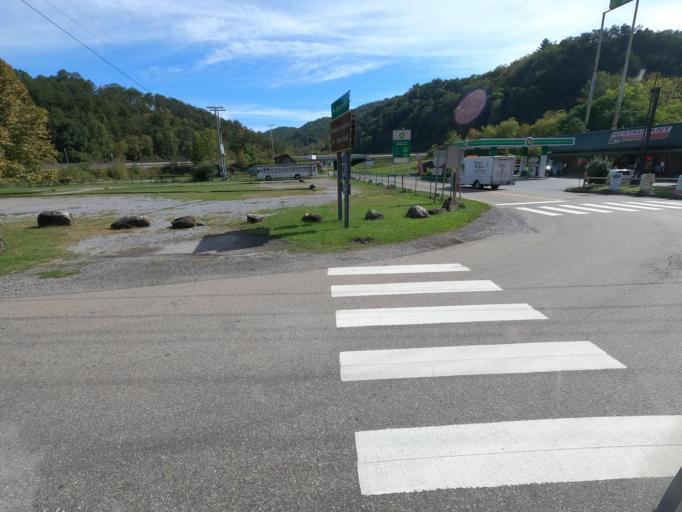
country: US
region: Tennessee
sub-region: Cocke County
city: Newport
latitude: 35.8166
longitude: -83.1448
